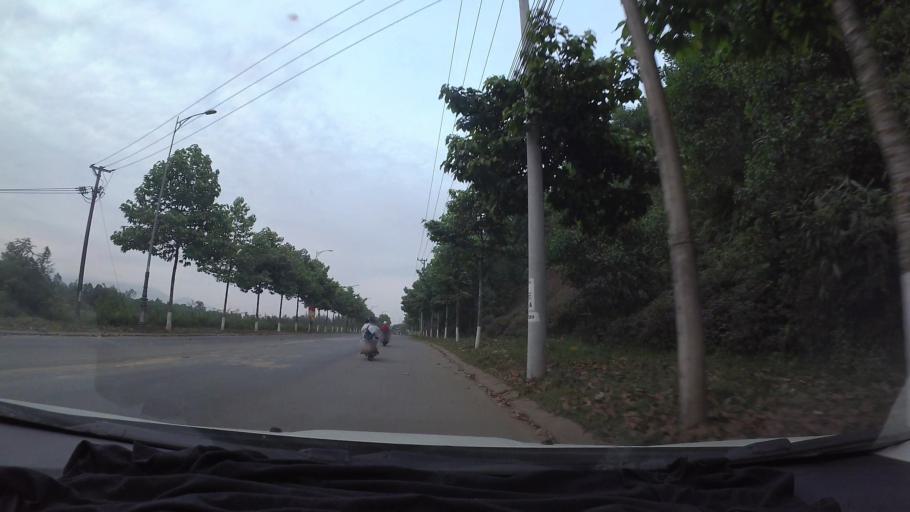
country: VN
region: Da Nang
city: Lien Chieu
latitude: 16.0604
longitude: 108.0983
